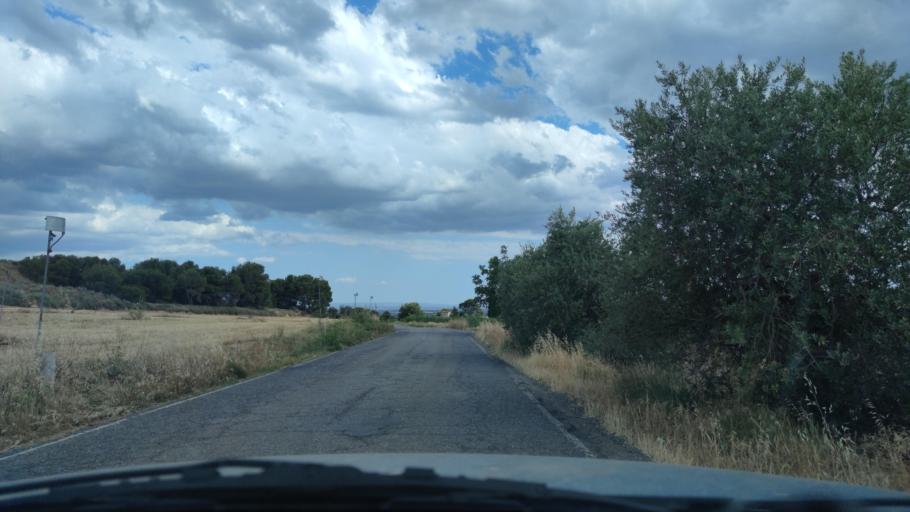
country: ES
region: Catalonia
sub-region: Provincia de Lleida
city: Lleida
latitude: 41.6040
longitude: 0.5855
